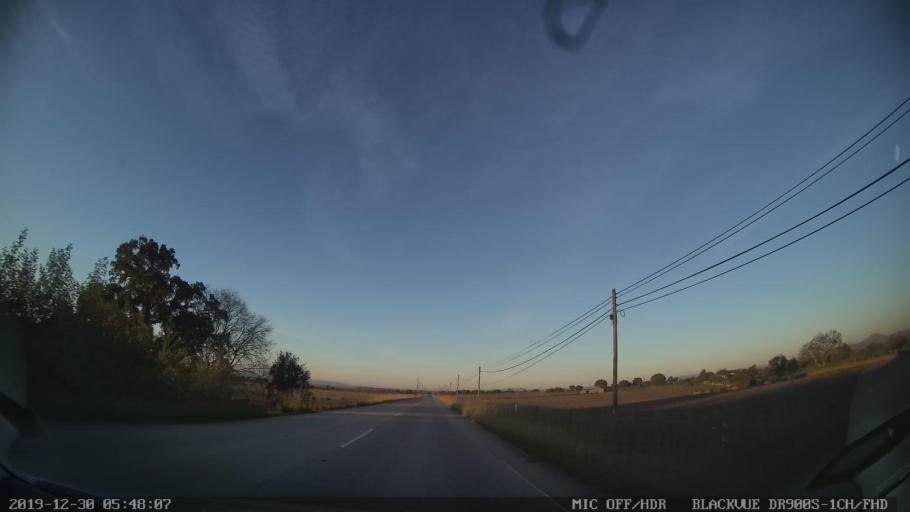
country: PT
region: Castelo Branco
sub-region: Idanha-A-Nova
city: Idanha-a-Nova
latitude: 39.9585
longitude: -7.2419
